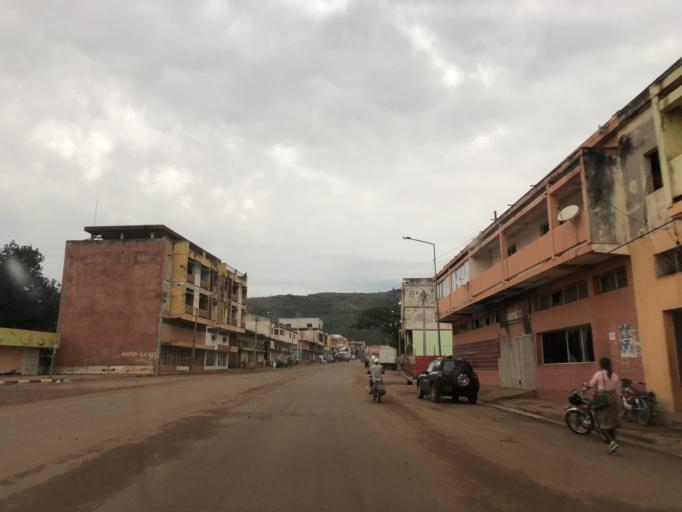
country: AO
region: Cuanza Sul
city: Uacu Cungo
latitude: -11.3577
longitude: 15.1214
